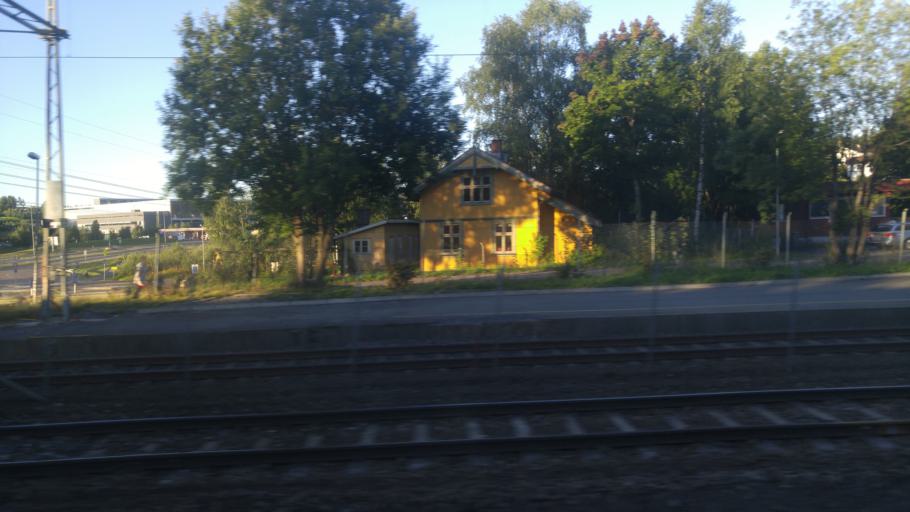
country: NO
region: Akershus
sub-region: Lorenskog
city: Kjenn
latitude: 59.9448
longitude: 10.9464
